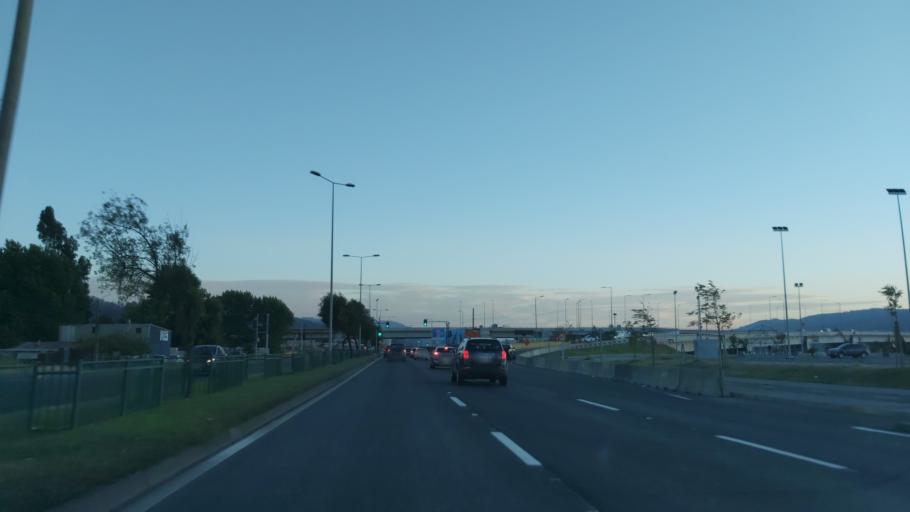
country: CL
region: Biobio
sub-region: Provincia de Concepcion
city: Concepcion
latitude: -36.8343
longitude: -73.0635
